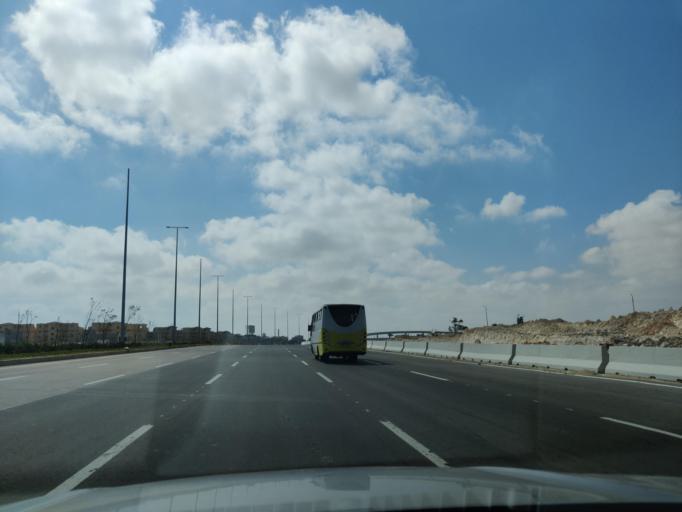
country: EG
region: Muhafazat Matruh
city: Al `Alamayn
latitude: 30.9574
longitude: 28.7645
